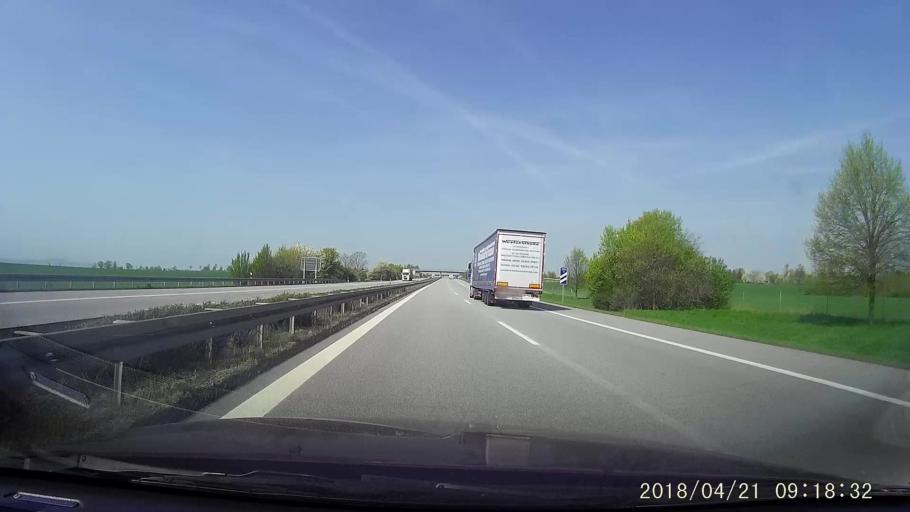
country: DE
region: Saxony
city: Weissenberg
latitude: 51.2057
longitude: 14.6738
